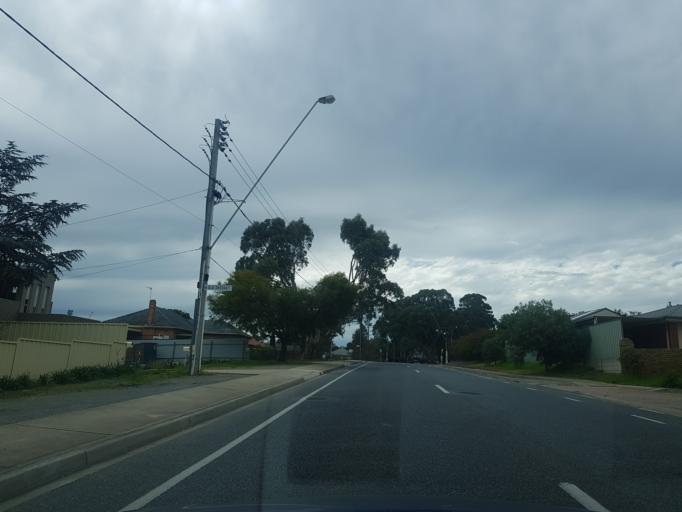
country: AU
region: South Australia
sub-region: Tea Tree Gully
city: Hope Valley
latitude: -34.8472
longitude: 138.7168
